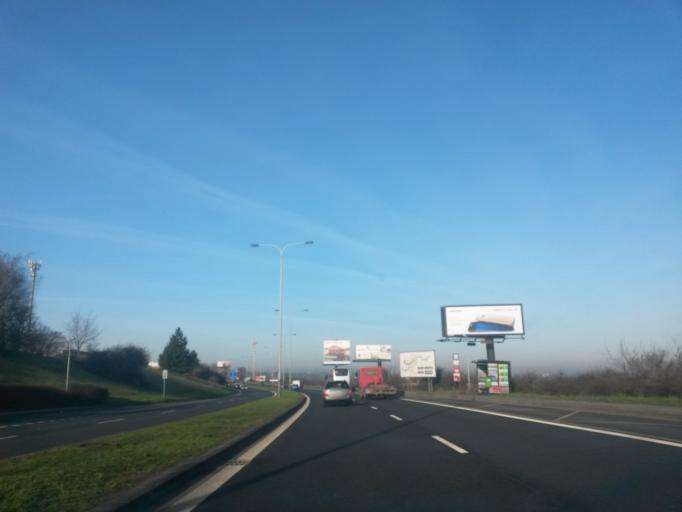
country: CZ
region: Praha
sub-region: Praha 12
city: Modrany
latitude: 50.0264
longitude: 14.3612
